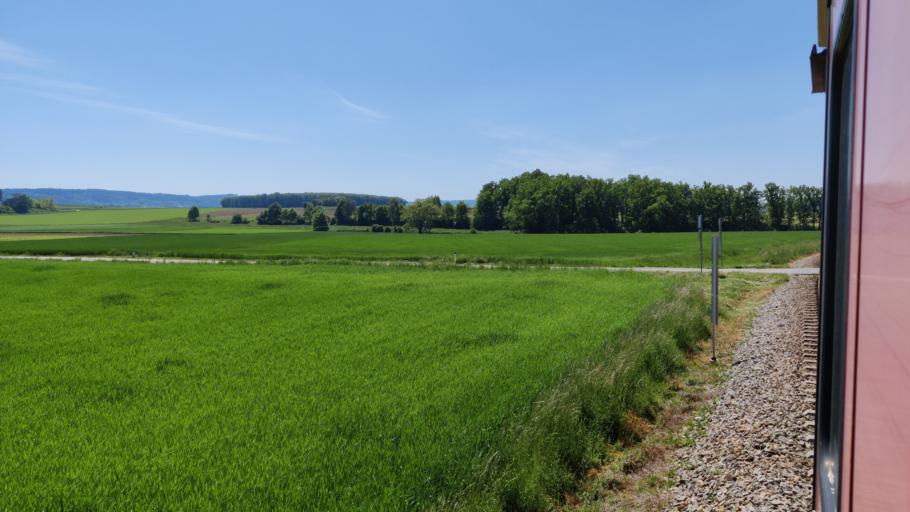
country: AT
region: Lower Austria
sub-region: Politischer Bezirk Horn
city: Horn
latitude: 48.6410
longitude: 15.6840
